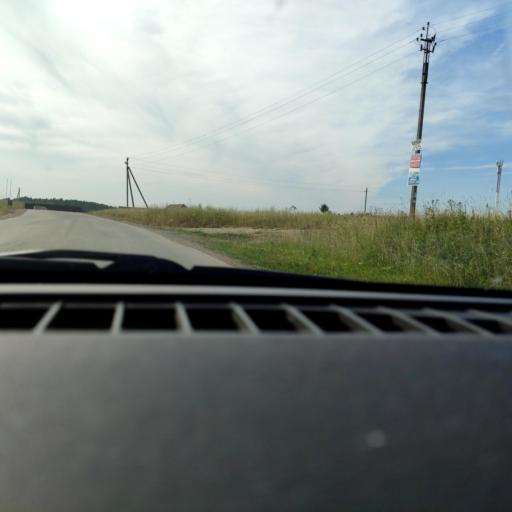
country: RU
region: Perm
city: Polazna
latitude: 58.3522
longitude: 56.2452
